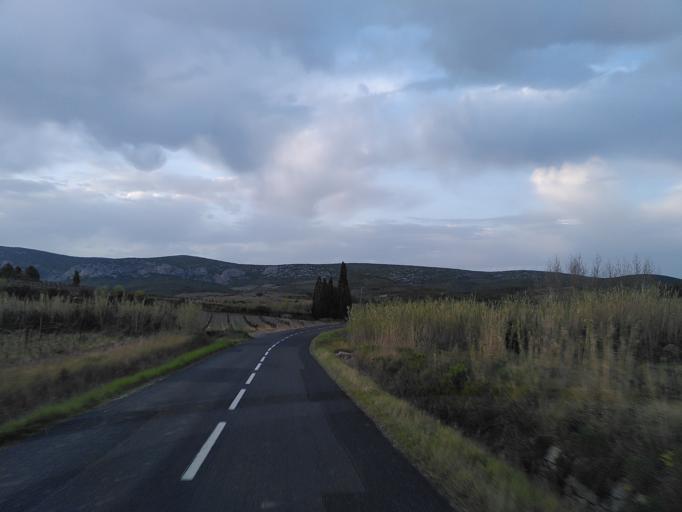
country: FR
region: Languedoc-Roussillon
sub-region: Departement des Pyrenees-Orientales
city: Estagel
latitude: 42.8115
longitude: 2.6988
